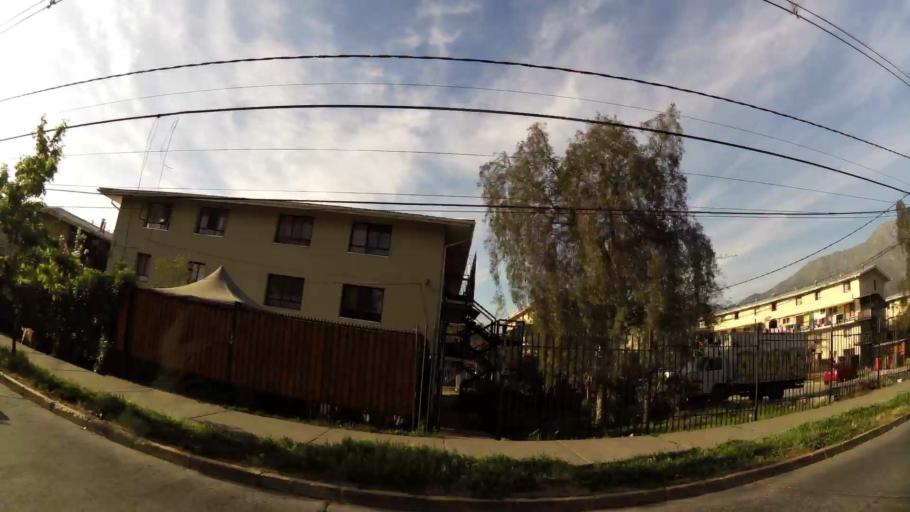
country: CL
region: Santiago Metropolitan
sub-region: Provincia de Santiago
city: Villa Presidente Frei, Nunoa, Santiago, Chile
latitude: -33.4767
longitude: -70.5383
